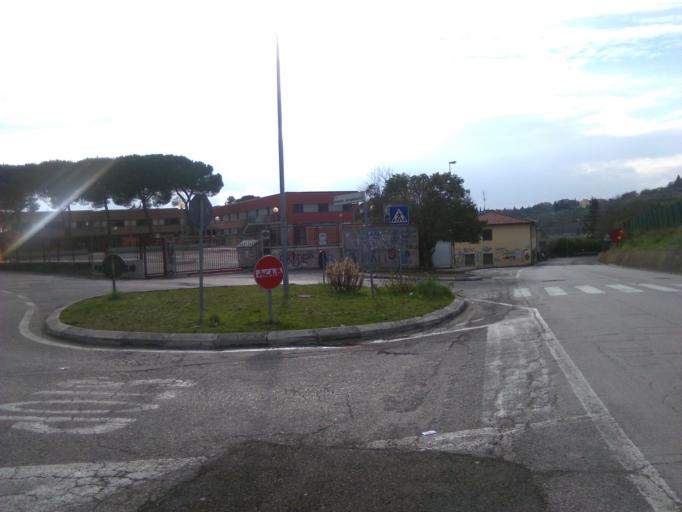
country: IT
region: Umbria
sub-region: Provincia di Perugia
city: Lacugnano
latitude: 43.0944
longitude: 12.3606
